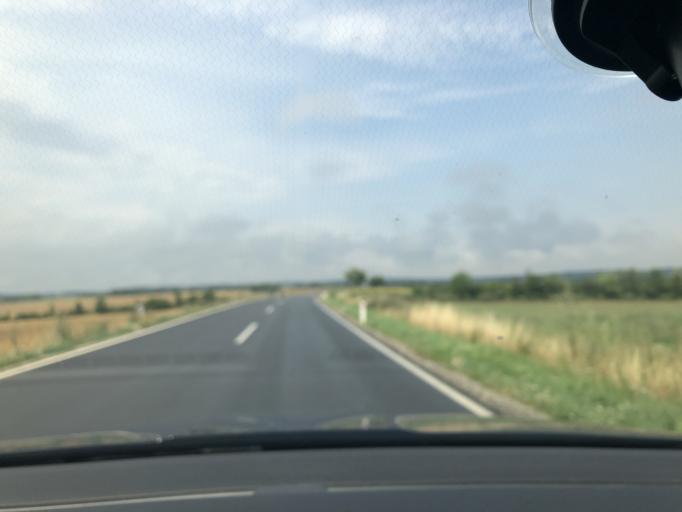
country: AT
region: Lower Austria
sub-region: Politischer Bezirk Mistelbach
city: Gaweinstal
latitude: 48.4876
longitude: 16.5710
